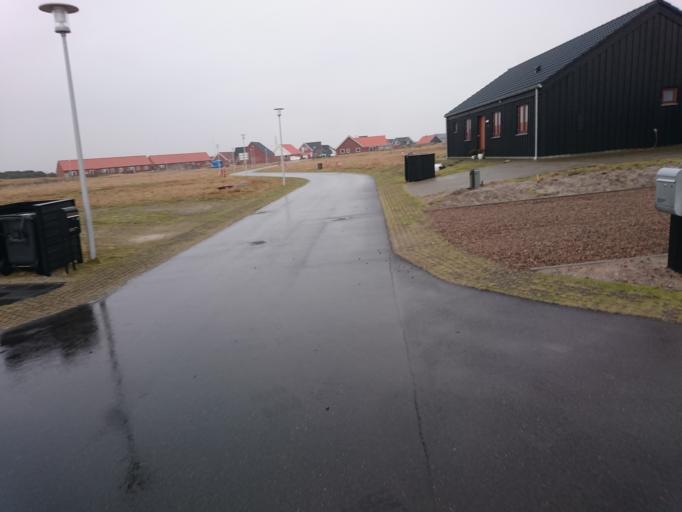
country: DK
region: South Denmark
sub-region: Fano Kommune
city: Nordby
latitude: 55.4444
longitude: 8.3854
